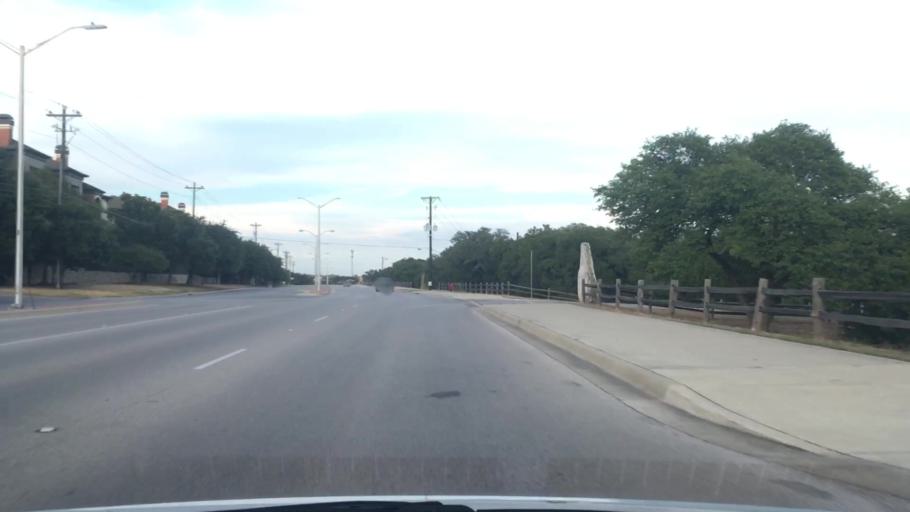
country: US
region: Texas
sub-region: Williamson County
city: Brushy Creek
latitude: 30.5089
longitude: -97.7732
